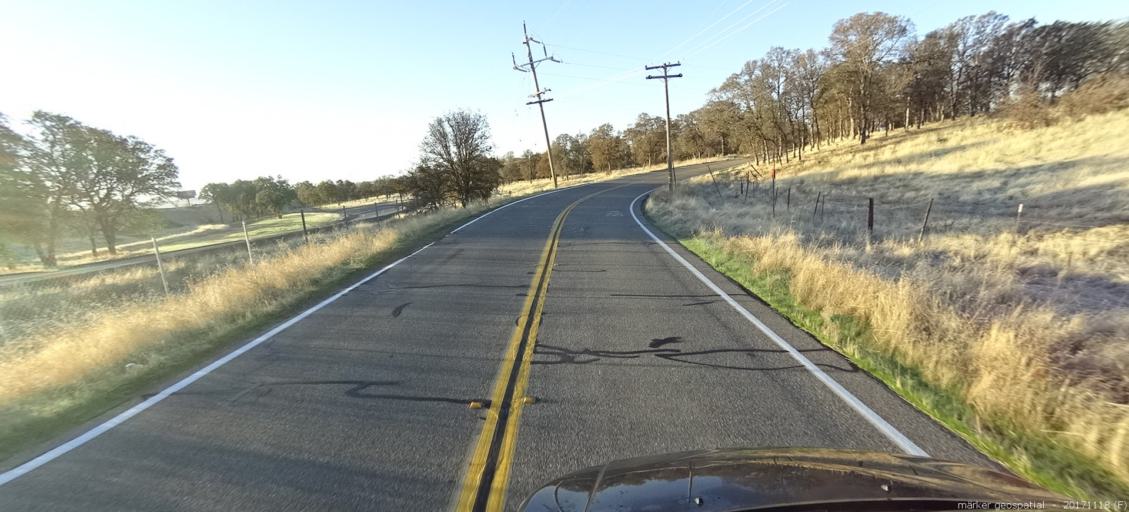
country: US
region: California
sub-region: Shasta County
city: Cottonwood
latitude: 40.4061
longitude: -122.2821
